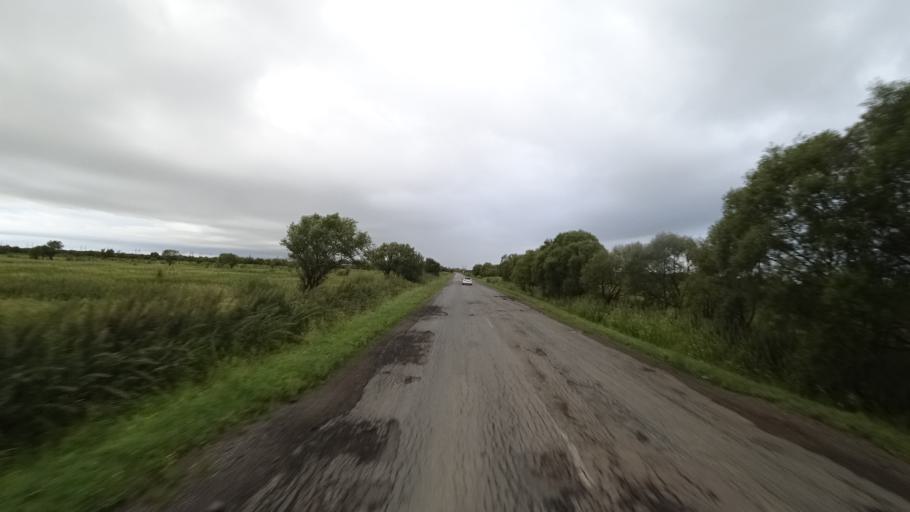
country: RU
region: Primorskiy
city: Chernigovka
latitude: 44.3598
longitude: 132.5569
